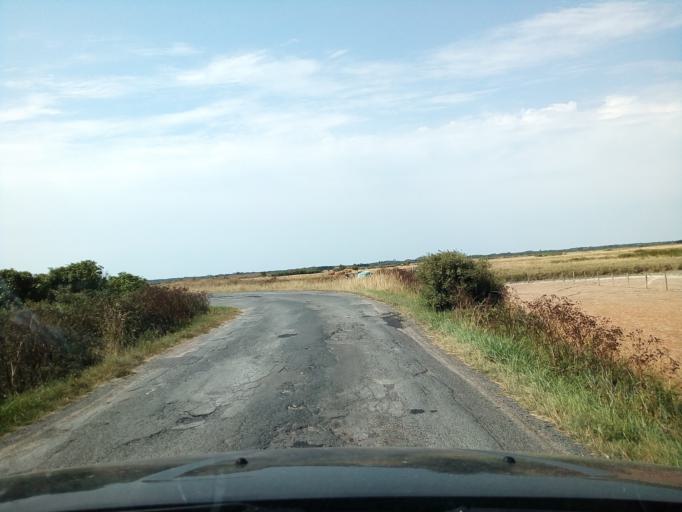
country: FR
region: Poitou-Charentes
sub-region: Departement de la Charente-Maritime
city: Boyard-Ville
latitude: 45.9546
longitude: -1.2638
